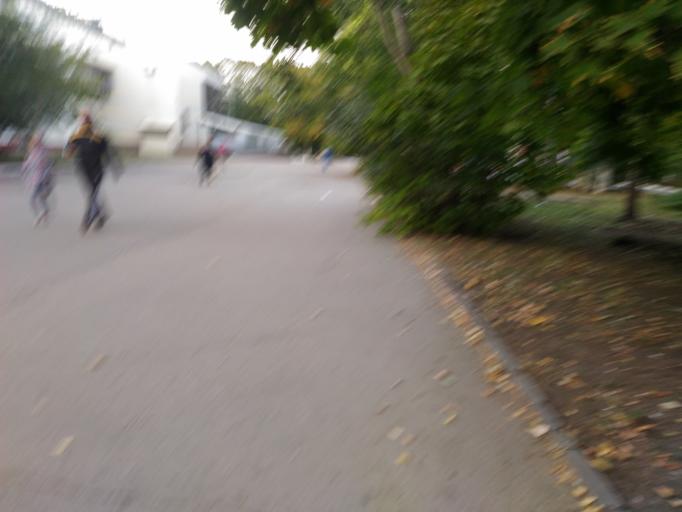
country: RU
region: Ulyanovsk
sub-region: Ulyanovskiy Rayon
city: Ulyanovsk
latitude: 54.3021
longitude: 48.3301
